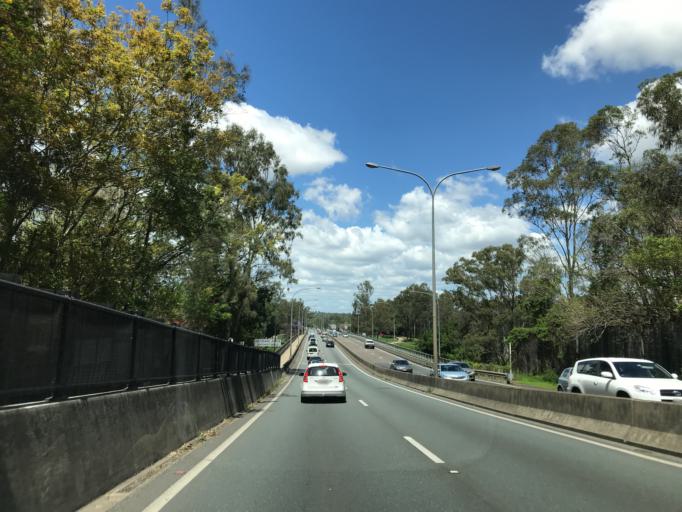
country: AU
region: Queensland
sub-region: Brisbane
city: Kenmore Hills
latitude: -27.5259
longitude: 152.9474
